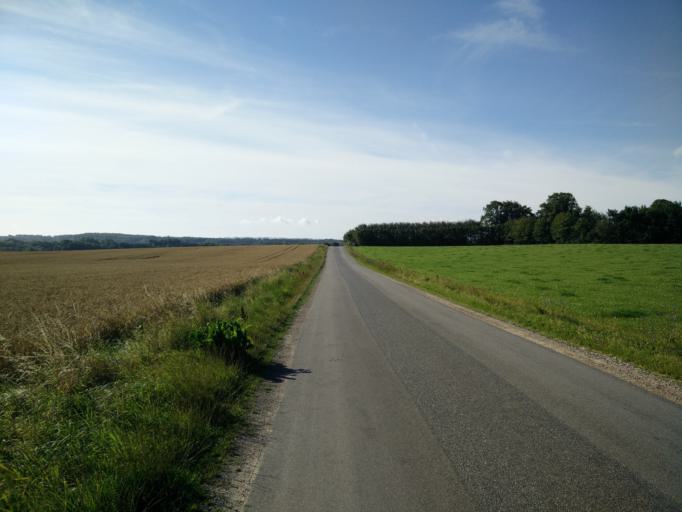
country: DK
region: Central Jutland
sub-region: Syddjurs Kommune
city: Ronde
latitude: 56.3048
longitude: 10.4416
